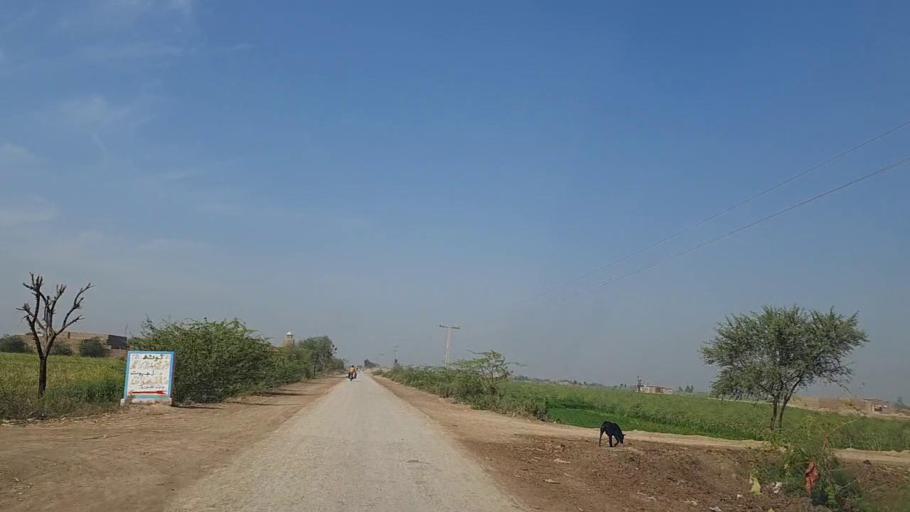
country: PK
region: Sindh
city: Mirpur Khas
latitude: 25.4824
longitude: 69.0002
